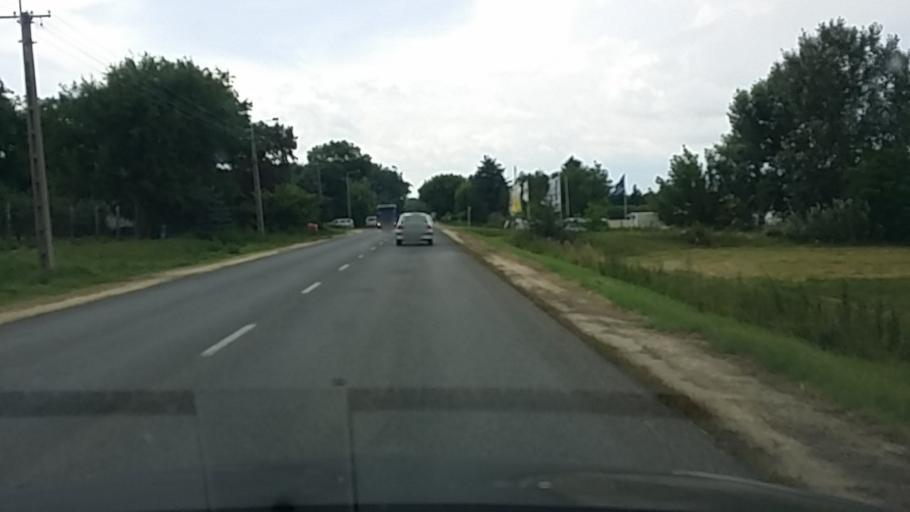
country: HU
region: Pest
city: Orkeny
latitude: 47.1223
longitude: 19.4370
